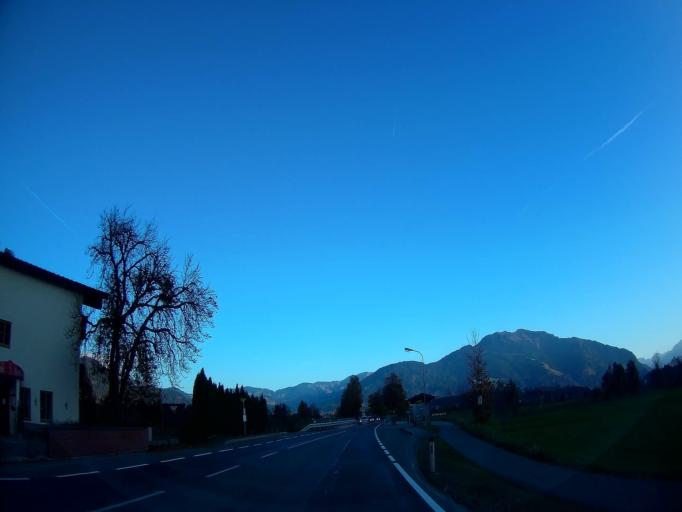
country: AT
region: Salzburg
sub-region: Politischer Bezirk Zell am See
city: Saalfelden am Steinernen Meer
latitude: 47.4387
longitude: 12.8201
